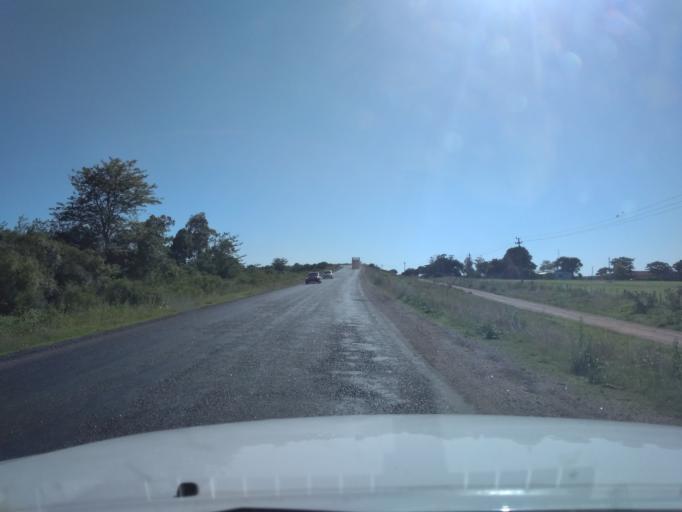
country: UY
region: Canelones
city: San Ramon
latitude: -34.2676
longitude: -55.9332
